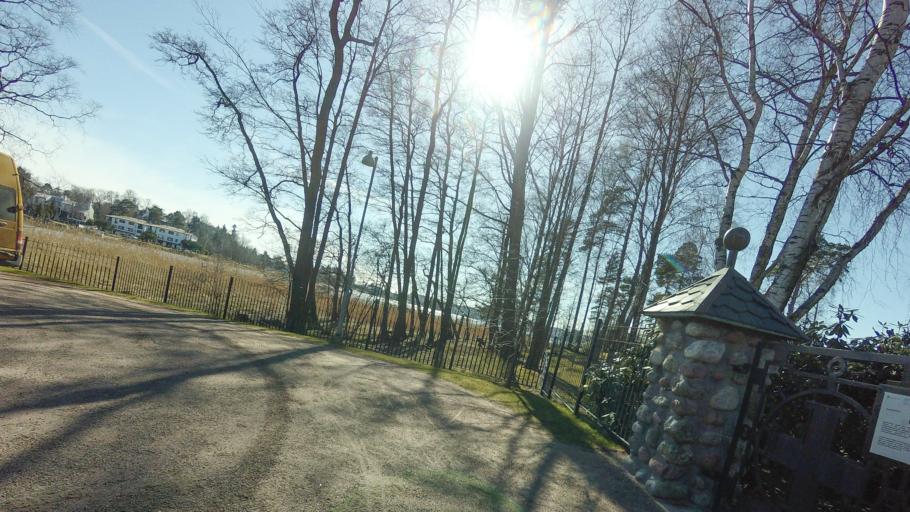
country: FI
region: Uusimaa
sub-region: Helsinki
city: Helsinki
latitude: 60.1906
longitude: 25.0011
